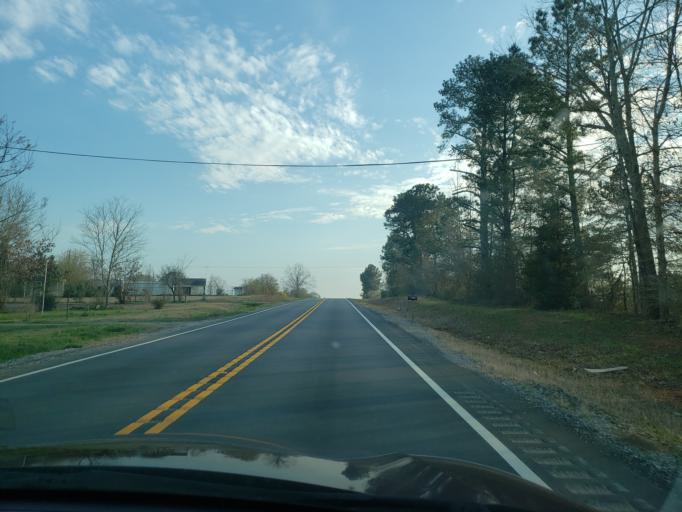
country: US
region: Alabama
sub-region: Hale County
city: Moundville
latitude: 32.8795
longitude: -87.6091
